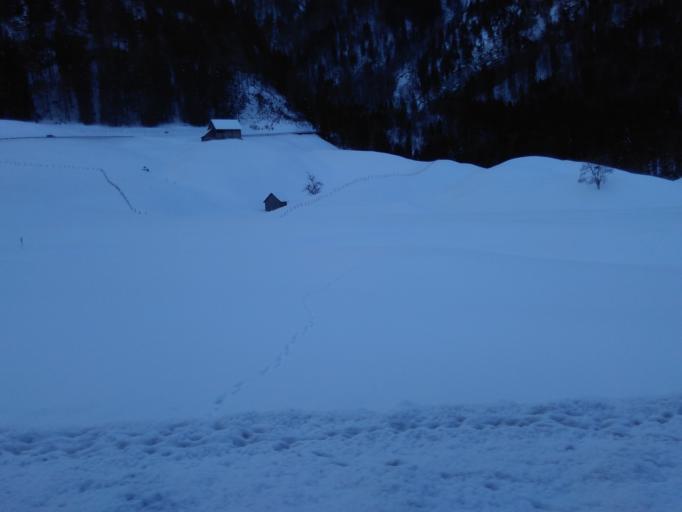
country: CH
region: Schwyz
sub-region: Bezirk March
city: Vorderthal
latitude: 47.1162
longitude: 8.9046
